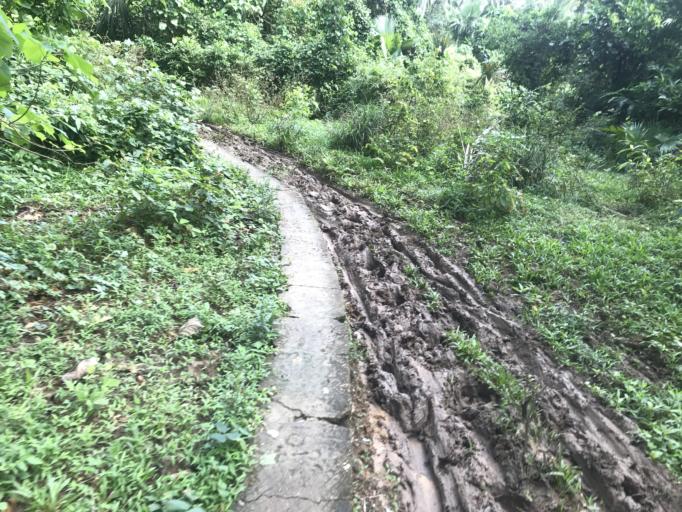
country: PH
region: Calabarzon
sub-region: Province of Quezon
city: Macalelon
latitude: 13.7821
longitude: 122.1411
